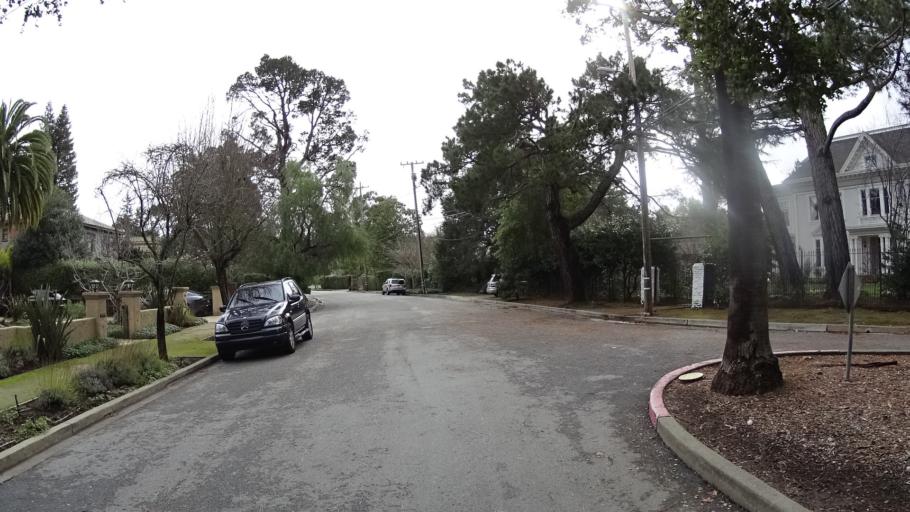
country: US
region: California
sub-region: San Mateo County
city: San Mateo
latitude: 37.5716
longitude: -122.3418
